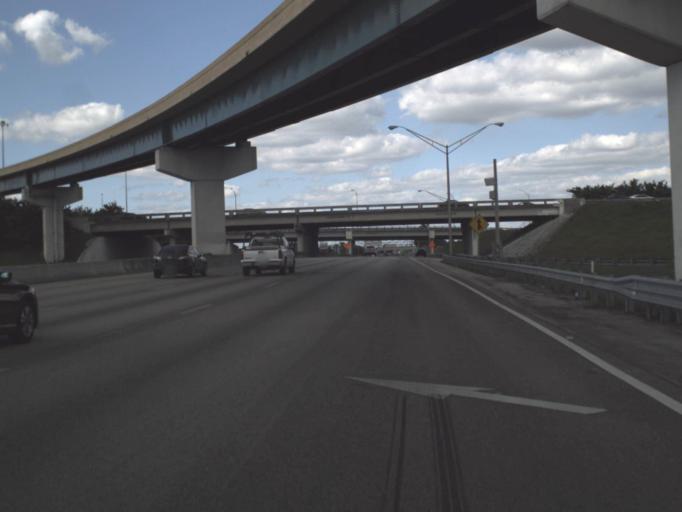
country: US
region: Florida
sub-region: Miami-Dade County
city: Lake Lucerne
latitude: 25.9709
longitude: -80.2295
